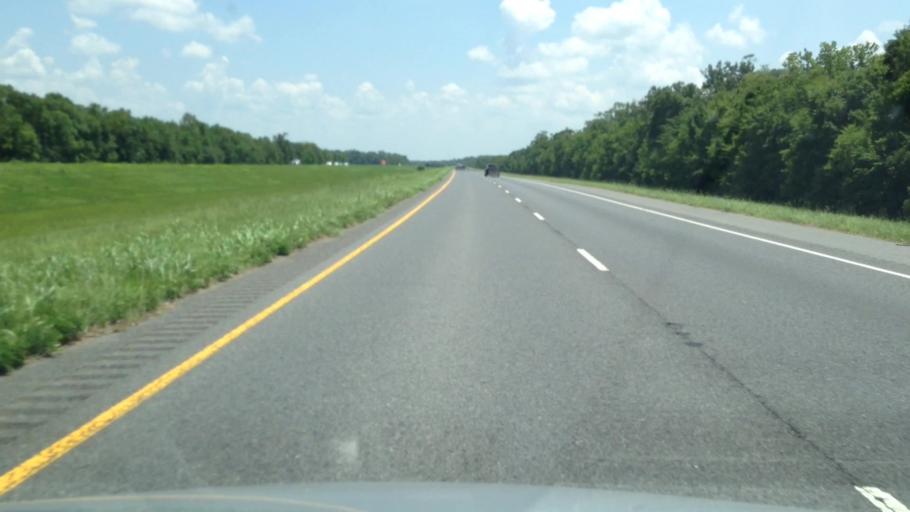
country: US
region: Louisiana
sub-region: Avoyelles Parish
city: Bunkie
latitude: 30.8310
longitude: -92.2272
